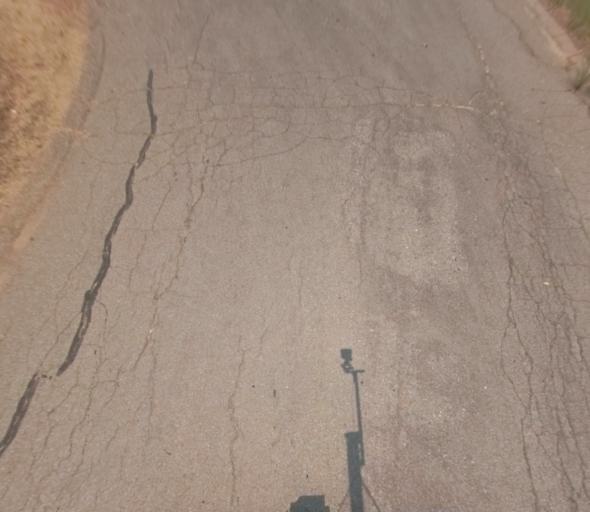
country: US
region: California
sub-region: Madera County
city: Oakhurst
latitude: 37.2547
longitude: -119.5702
